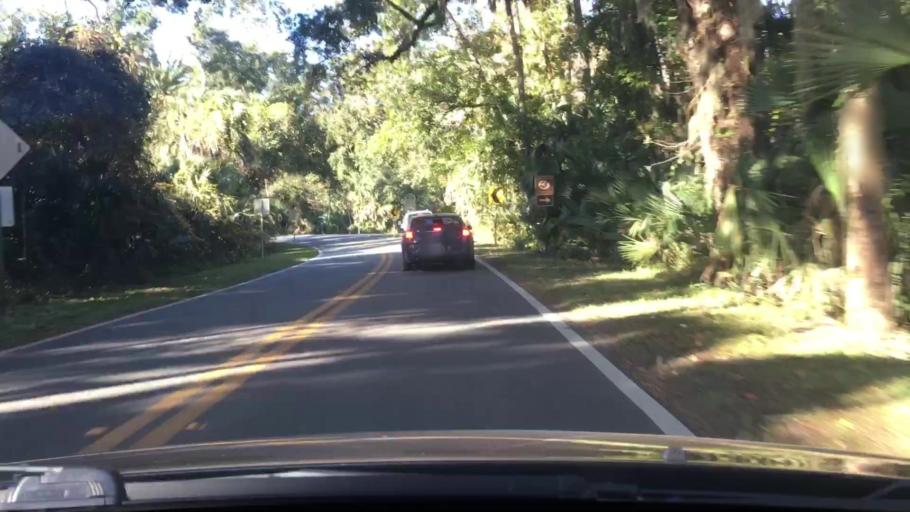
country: US
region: Florida
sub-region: Flagler County
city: Flagler Beach
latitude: 29.4024
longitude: -81.1372
